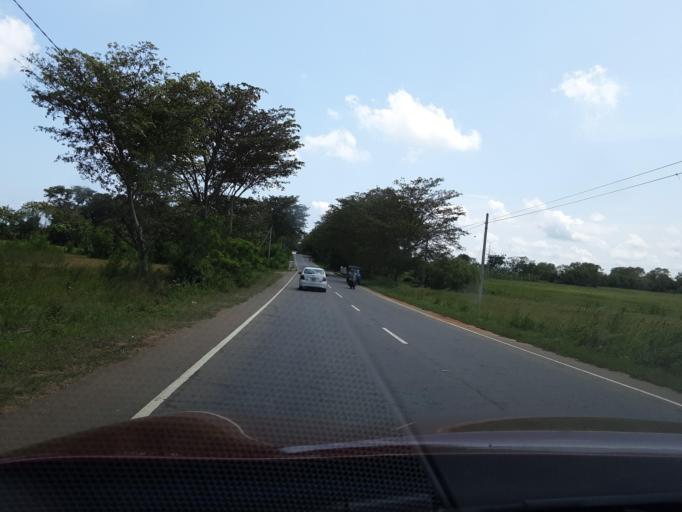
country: LK
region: Southern
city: Tangalla
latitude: 6.2303
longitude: 81.2247
